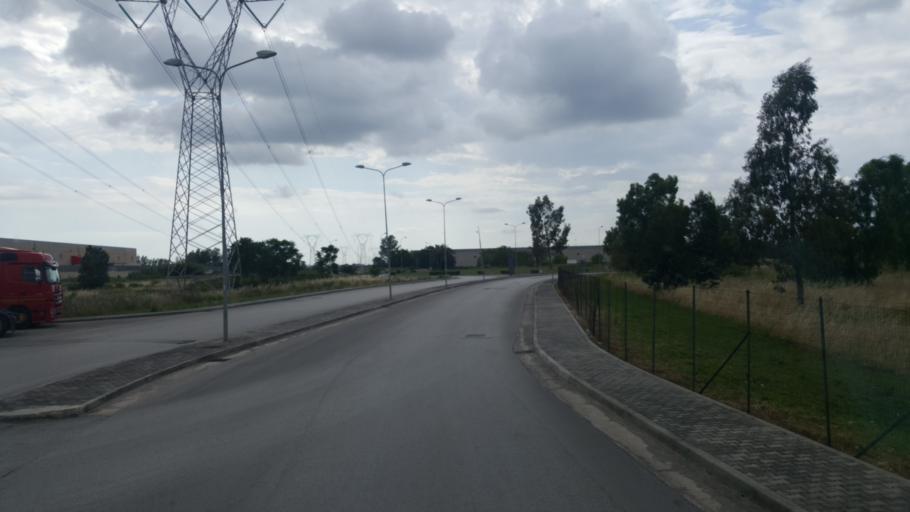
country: IT
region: Campania
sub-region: Provincia di Caserta
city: San Marco Evangelista
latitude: 41.0072
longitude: 14.3574
